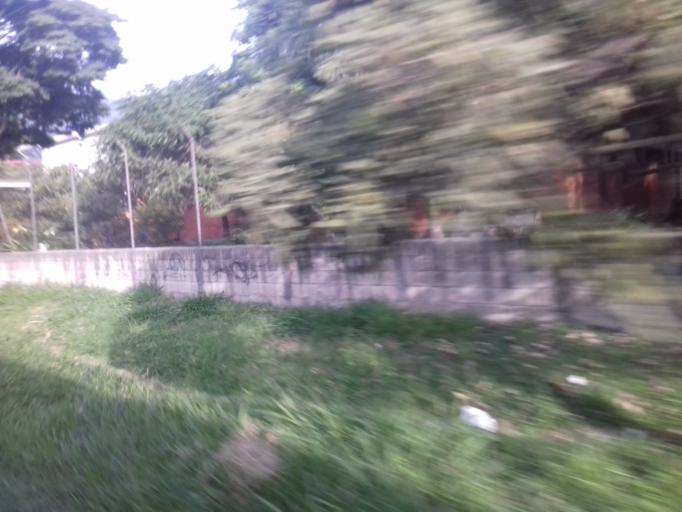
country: CO
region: Antioquia
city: Sabaneta
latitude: 6.1561
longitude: -75.6237
